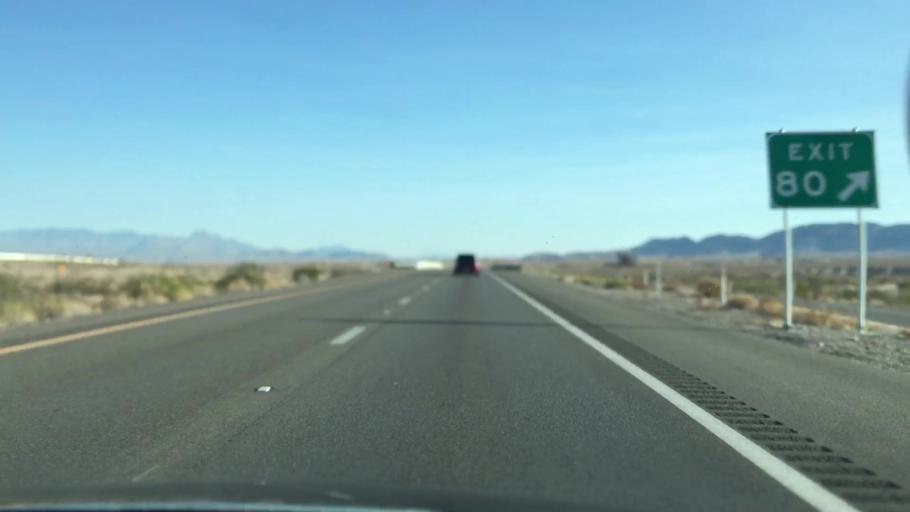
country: US
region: Nevada
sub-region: Clark County
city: Moapa Town
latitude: 36.5515
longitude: -114.6970
